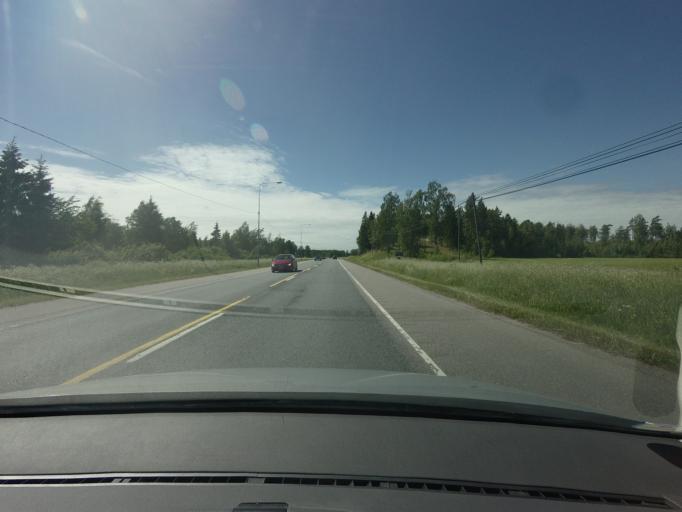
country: FI
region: Uusimaa
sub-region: Helsinki
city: Siuntio
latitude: 60.0950
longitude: 24.2462
